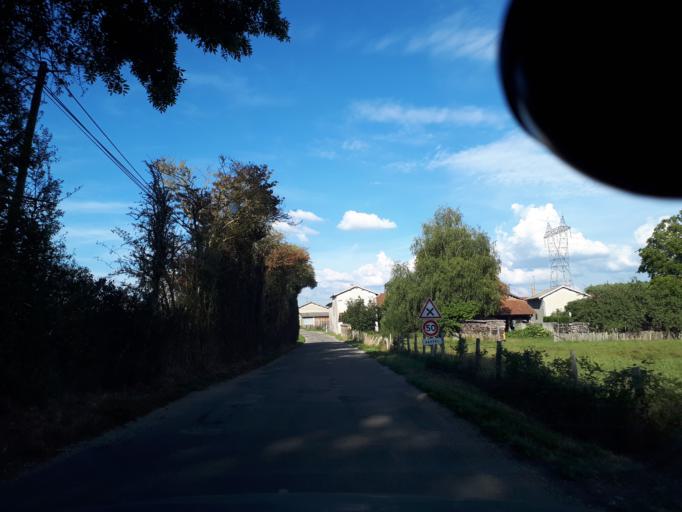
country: FR
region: Rhone-Alpes
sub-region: Departement de l'Isere
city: Chatonnay
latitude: 45.5182
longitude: 5.2431
